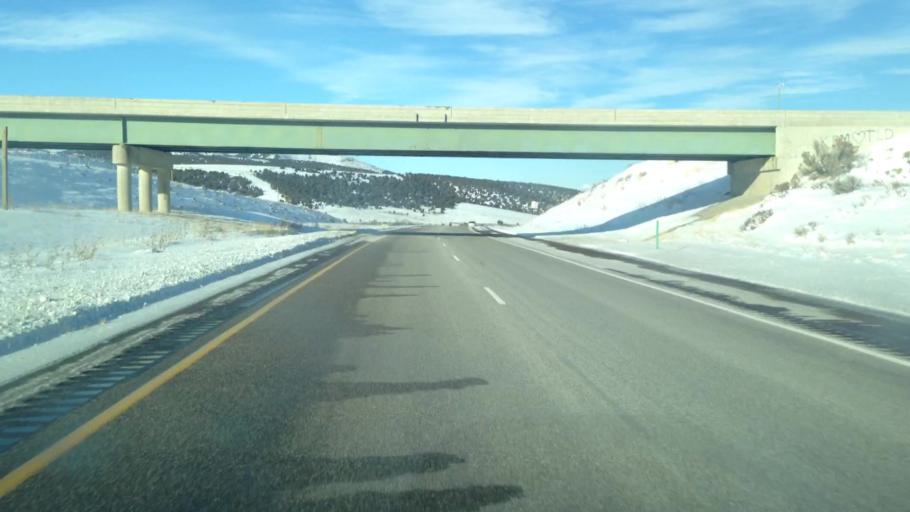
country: US
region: Idaho
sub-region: Oneida County
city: Malad City
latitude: 42.3430
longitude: -112.2265
